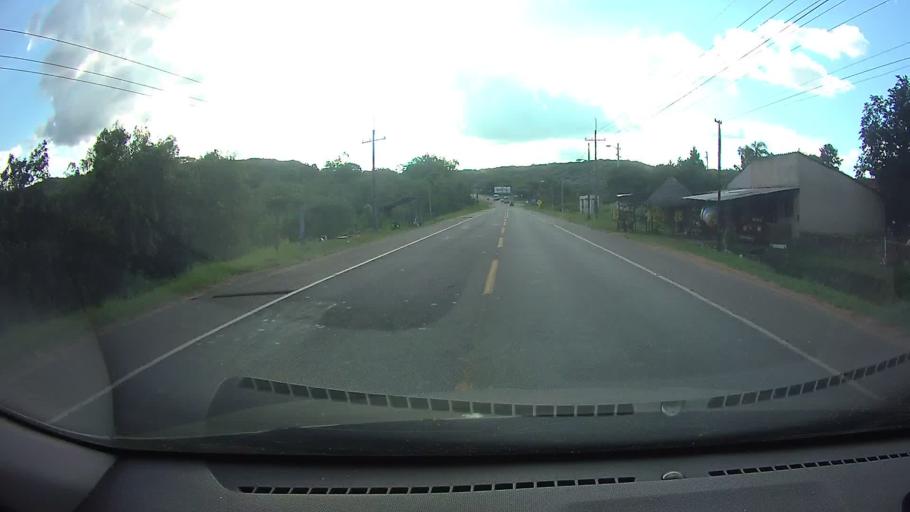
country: PY
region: Cordillera
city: Caacupe
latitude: -25.3894
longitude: -57.0817
